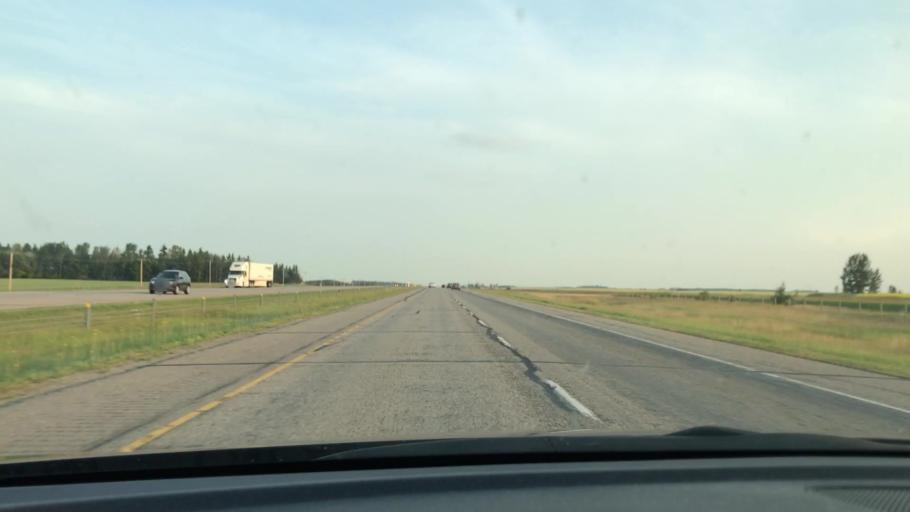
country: CA
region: Alberta
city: Olds
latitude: 51.8619
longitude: -114.0256
